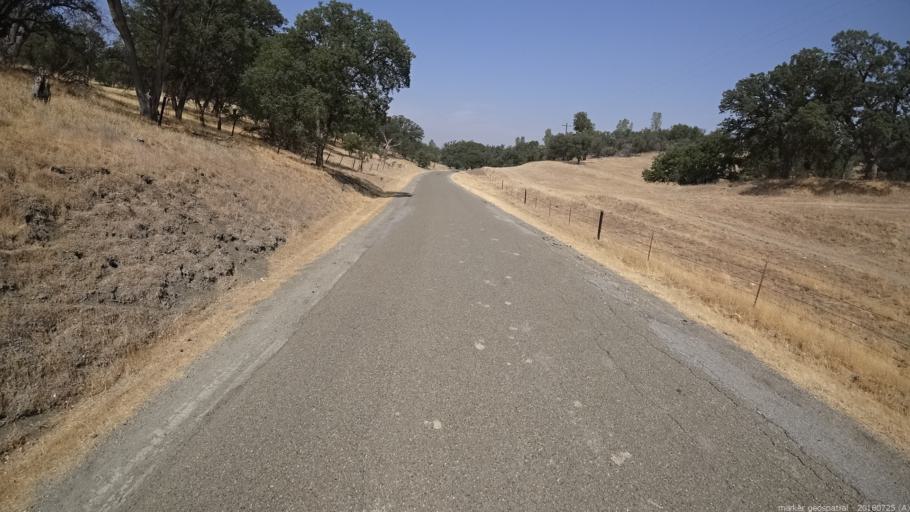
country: US
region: California
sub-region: San Luis Obispo County
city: Shandon
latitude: 35.8669
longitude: -120.4013
